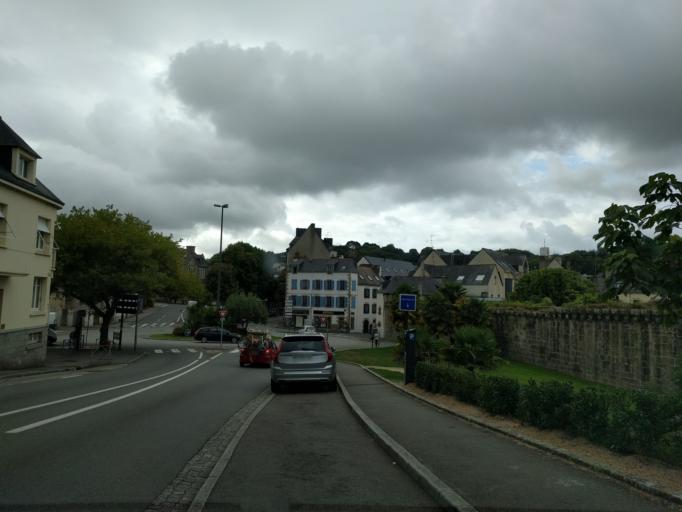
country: FR
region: Brittany
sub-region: Departement du Finistere
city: Quimper
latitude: 47.9976
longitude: -4.1010
